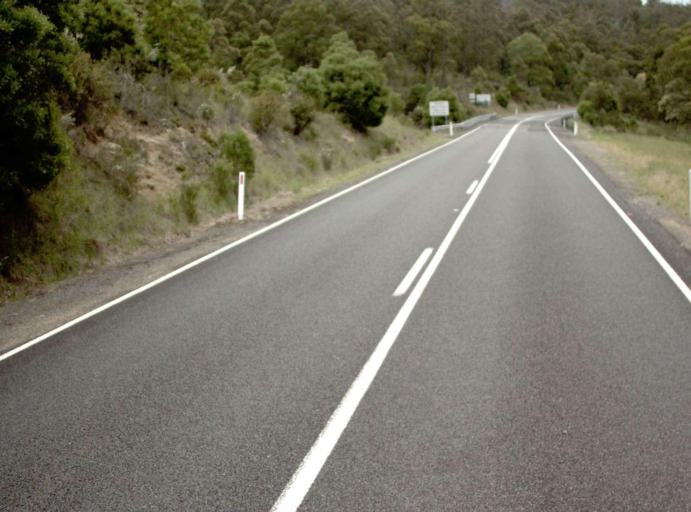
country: AU
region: New South Wales
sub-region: Bombala
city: Bombala
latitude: -37.2353
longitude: 149.2696
